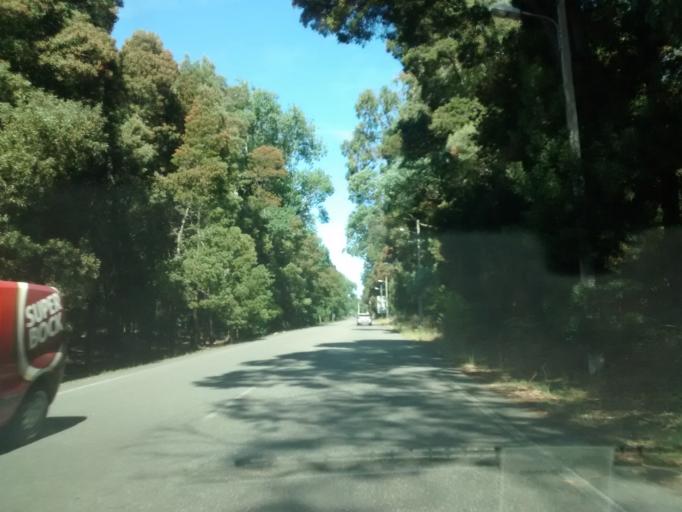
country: PT
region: Coimbra
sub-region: Mira
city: Mira
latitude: 40.4519
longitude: -8.7732
